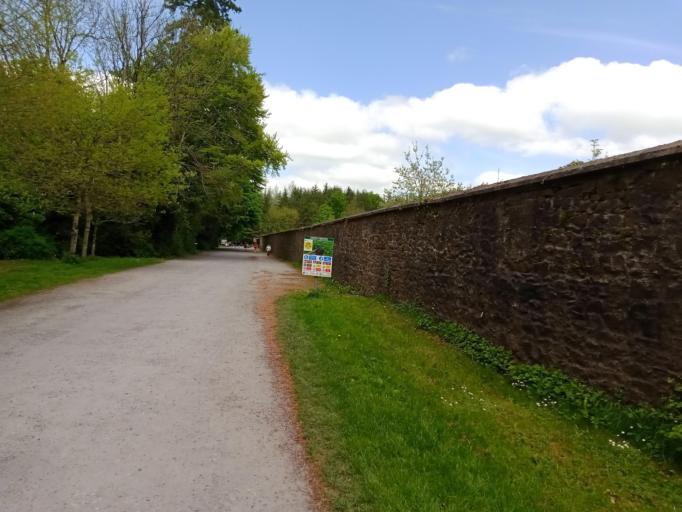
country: IE
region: Leinster
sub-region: Kilkenny
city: Castlecomer
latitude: 52.8077
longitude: -7.2031
